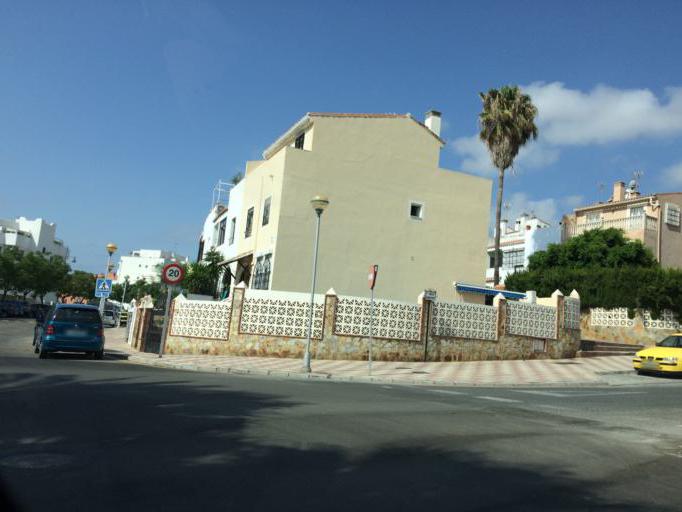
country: ES
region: Andalusia
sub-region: Provincia de Malaga
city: Torremolinos
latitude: 36.6381
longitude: -4.4926
